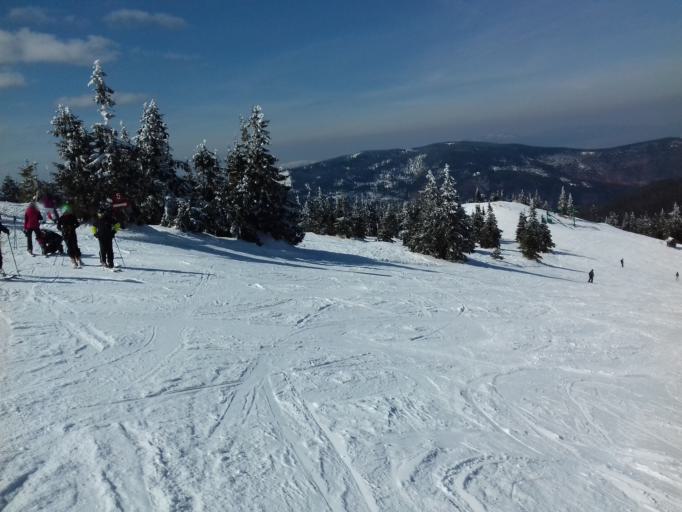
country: PL
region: Silesian Voivodeship
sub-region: Powiat zywiecki
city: Korbielow
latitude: 49.5355
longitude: 19.3178
